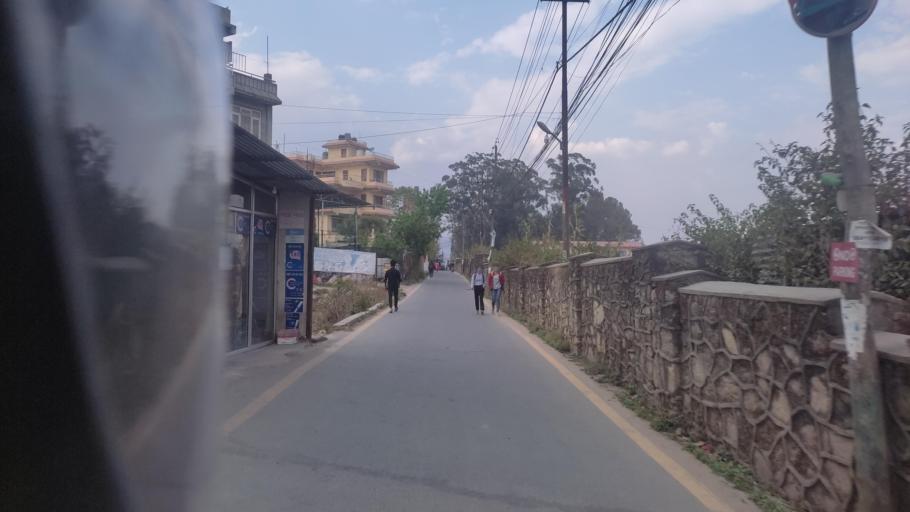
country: NP
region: Central Region
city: Kirtipur
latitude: 27.6791
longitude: 85.2817
